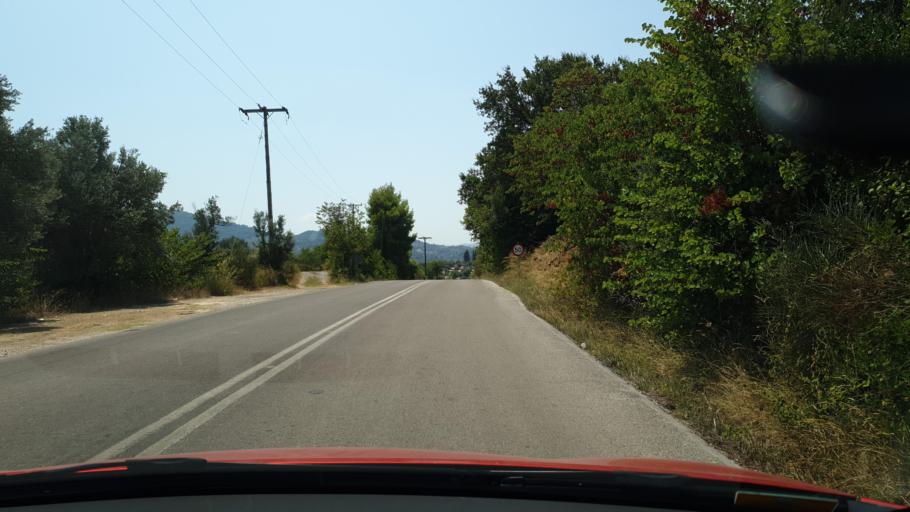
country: GR
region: Central Greece
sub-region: Nomos Evvoias
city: Kymi
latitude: 38.6118
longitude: 24.0796
